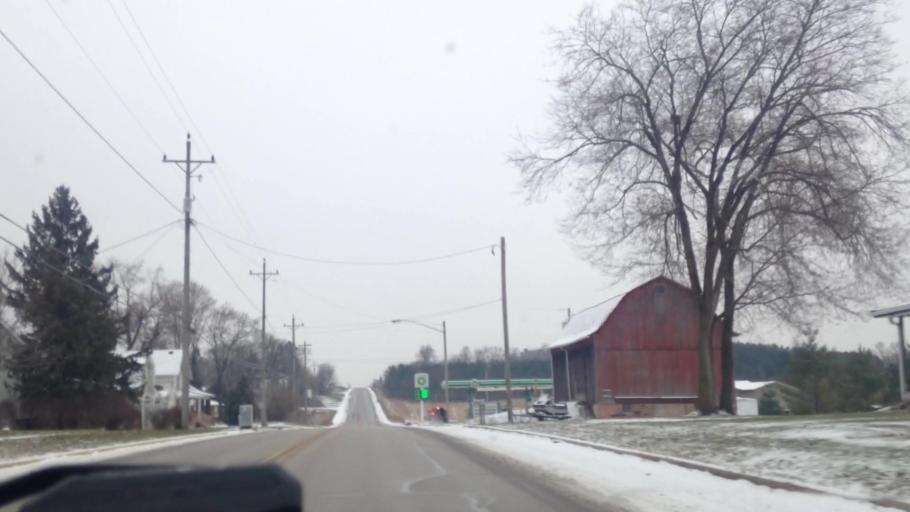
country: US
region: Wisconsin
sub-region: Dodge County
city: Hustisford
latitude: 43.3081
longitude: -88.5184
